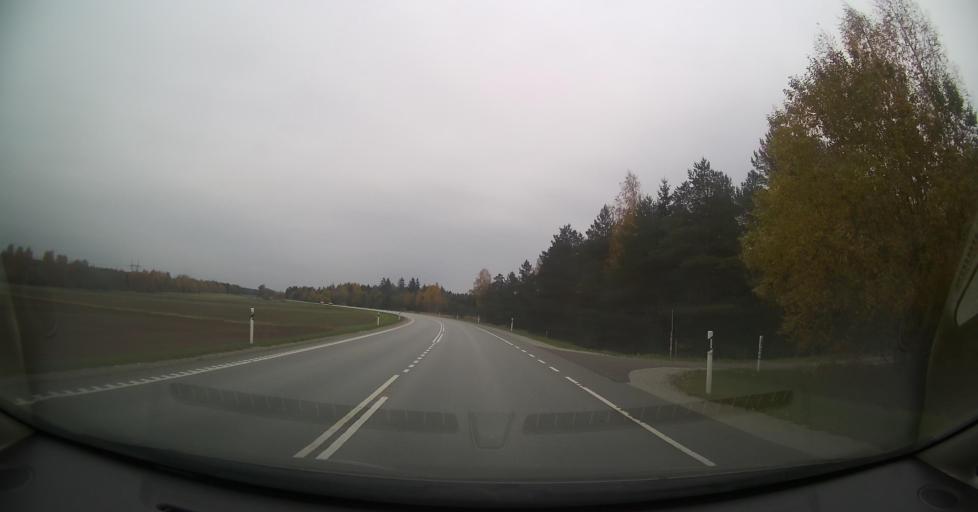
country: EE
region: Harju
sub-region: Nissi vald
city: Riisipere
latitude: 59.1320
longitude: 24.3183
